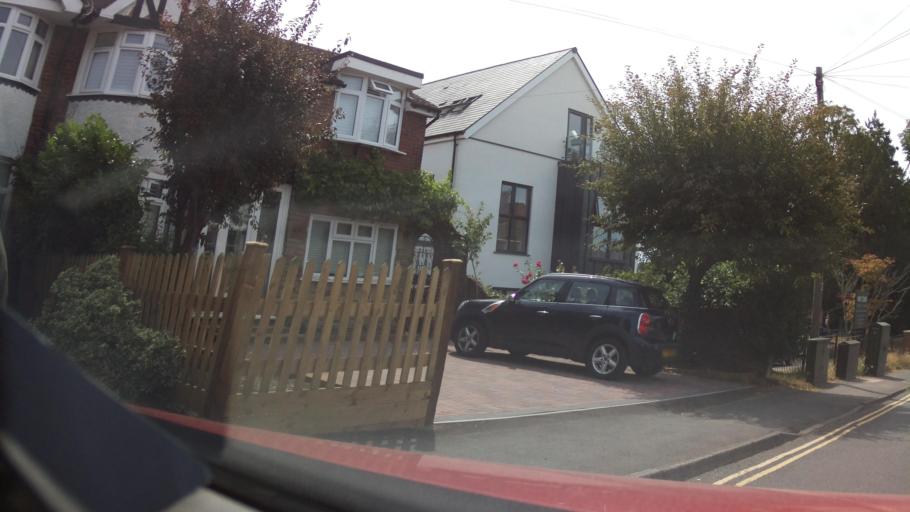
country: GB
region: England
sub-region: Surrey
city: Dorking
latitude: 51.2353
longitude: -0.3359
